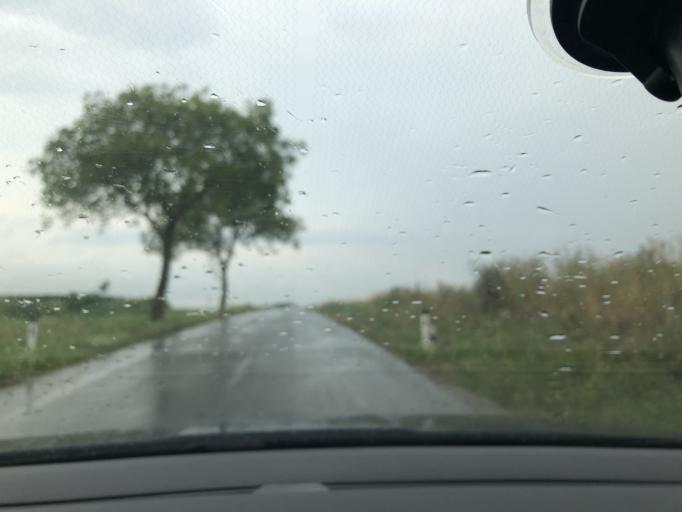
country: AT
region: Lower Austria
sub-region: Politischer Bezirk Ganserndorf
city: Auersthal
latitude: 48.3761
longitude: 16.6442
